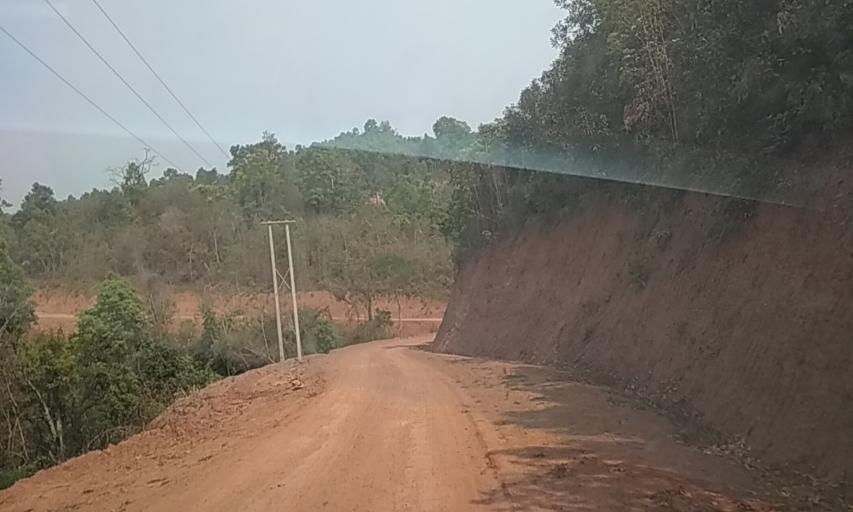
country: VN
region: Huyen Dien Bien
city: Dien Bien Phu
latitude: 21.4690
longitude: 102.7720
